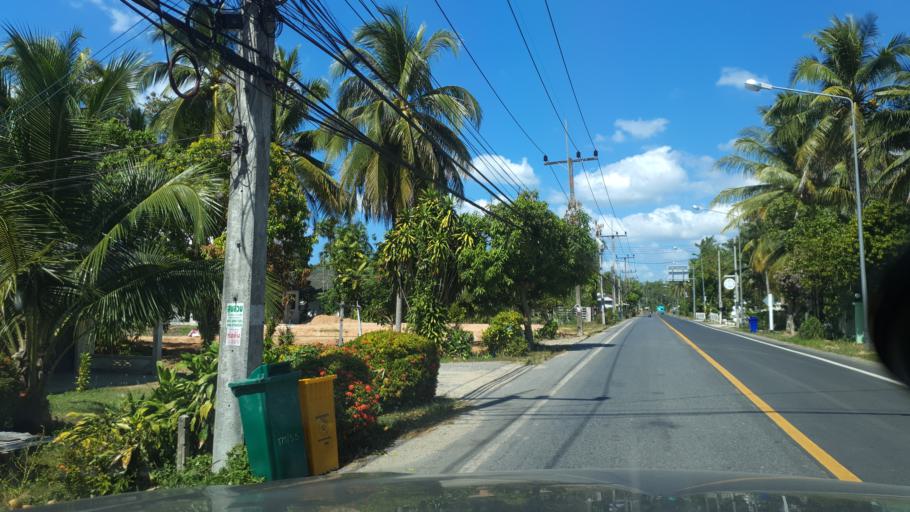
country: TH
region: Phuket
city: Thalang
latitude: 8.1355
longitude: 98.3069
